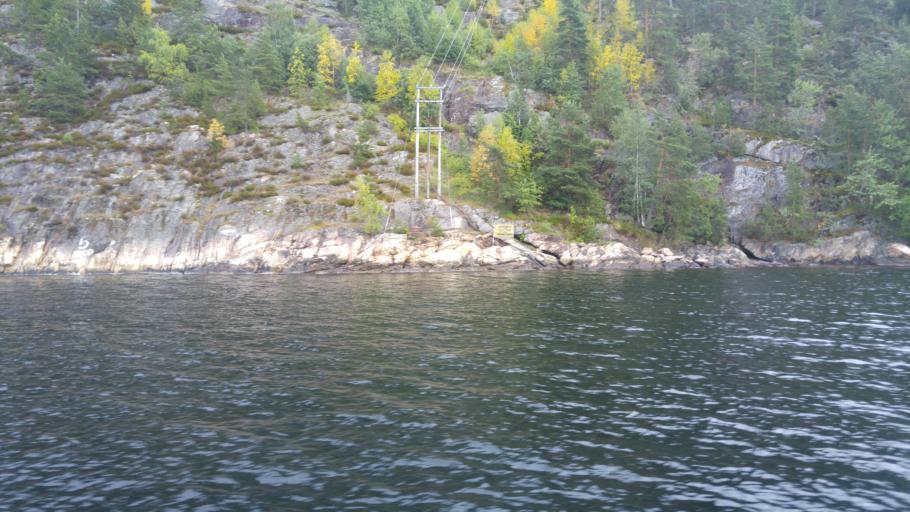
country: NO
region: Akershus
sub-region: Nesodden
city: Nesoddtangen
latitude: 59.8161
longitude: 10.6165
